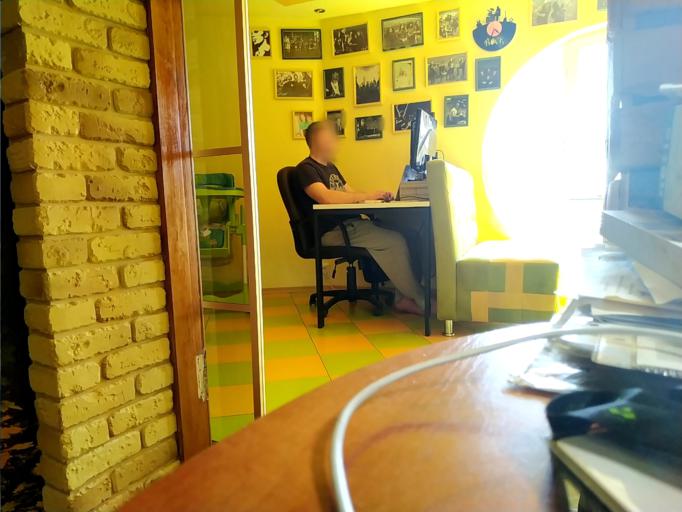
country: RU
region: Moskovskaya
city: Pavlovskiy Posad
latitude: 55.7475
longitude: 38.7253
